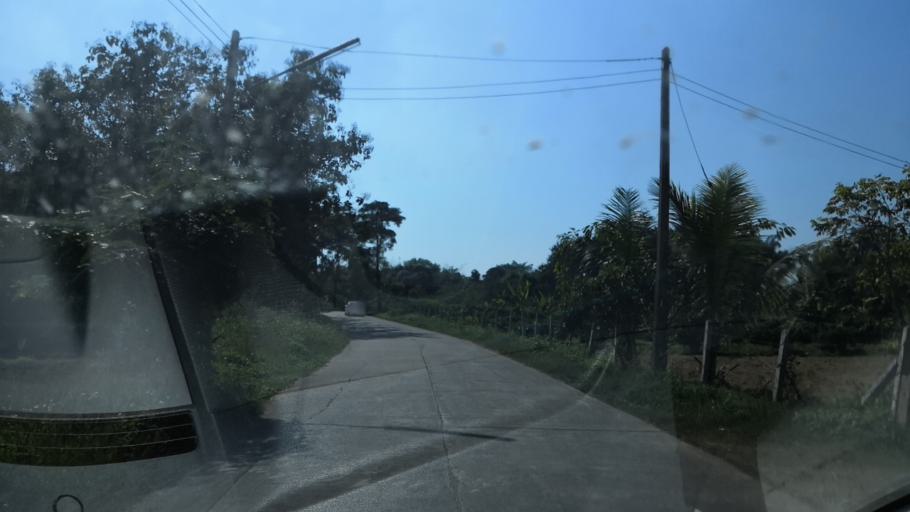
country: TH
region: Chiang Rai
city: Wiang Chai
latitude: 19.8828
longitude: 99.9423
